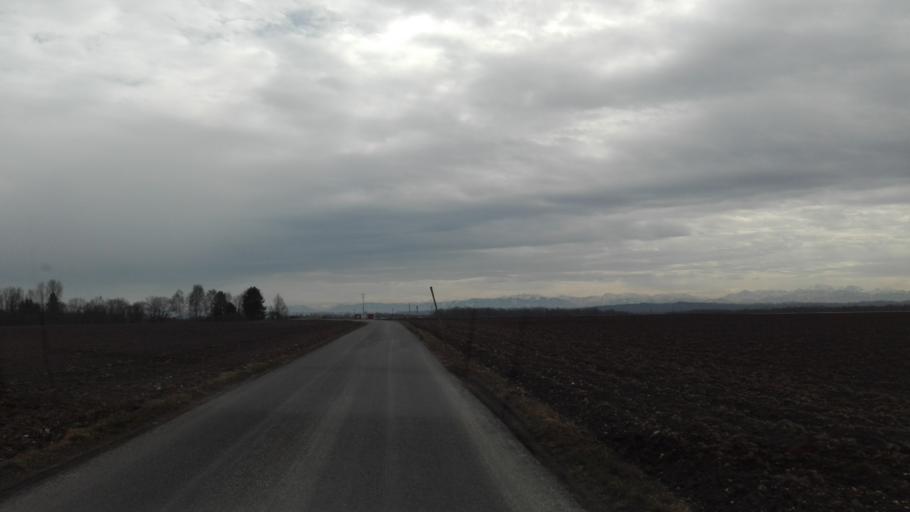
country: AT
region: Upper Austria
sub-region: Politischer Bezirk Linz-Land
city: Pasching
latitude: 48.2393
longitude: 14.2115
